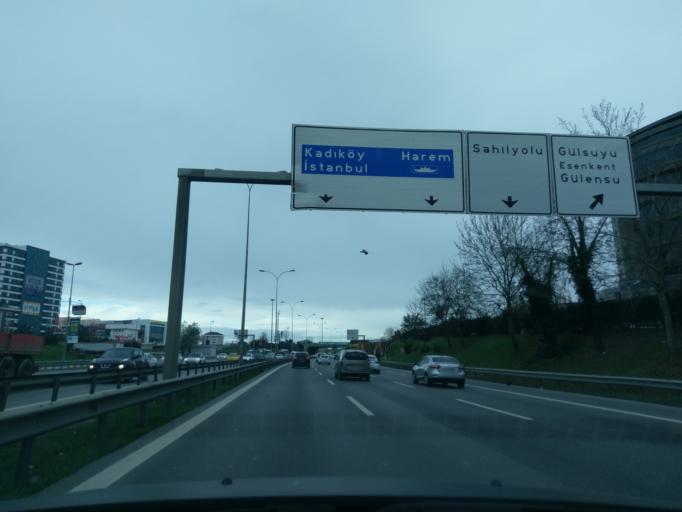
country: TR
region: Istanbul
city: Maltepe
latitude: 40.9239
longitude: 29.1555
